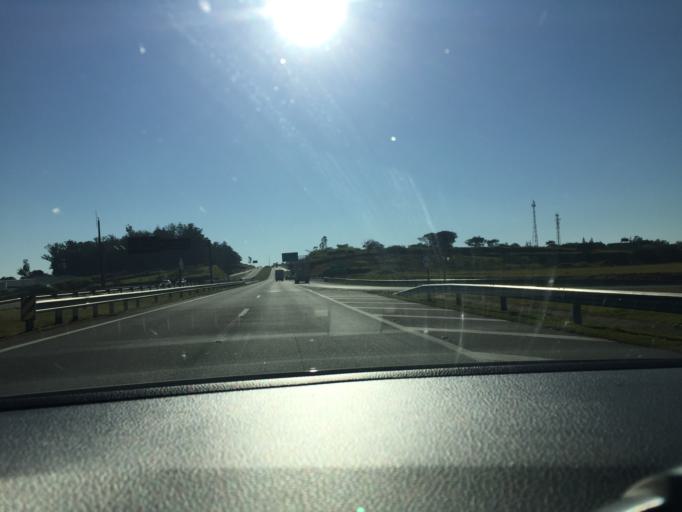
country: BR
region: Sao Paulo
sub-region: Valinhos
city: Valinhos
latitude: -22.9817
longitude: -47.0462
